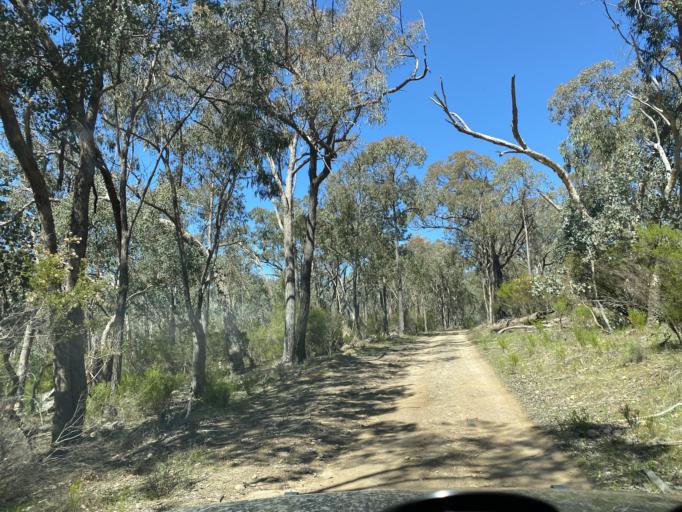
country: AU
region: Victoria
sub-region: Benalla
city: Benalla
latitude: -36.6985
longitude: 146.1522
